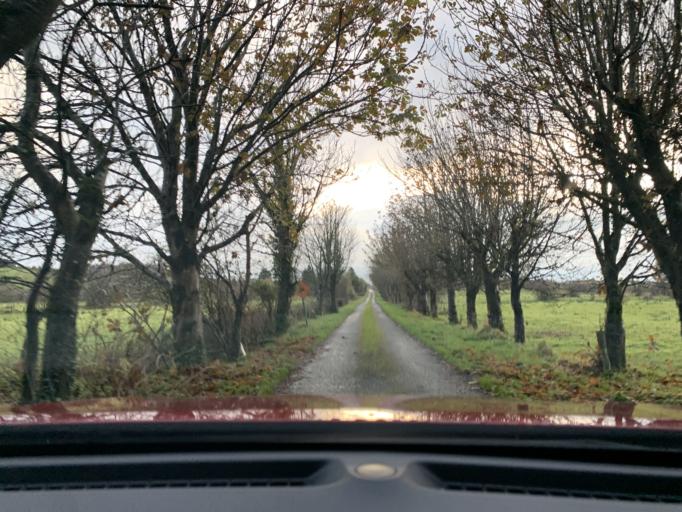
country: IE
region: Connaught
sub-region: Sligo
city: Ballymote
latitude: 54.0337
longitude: -8.5349
